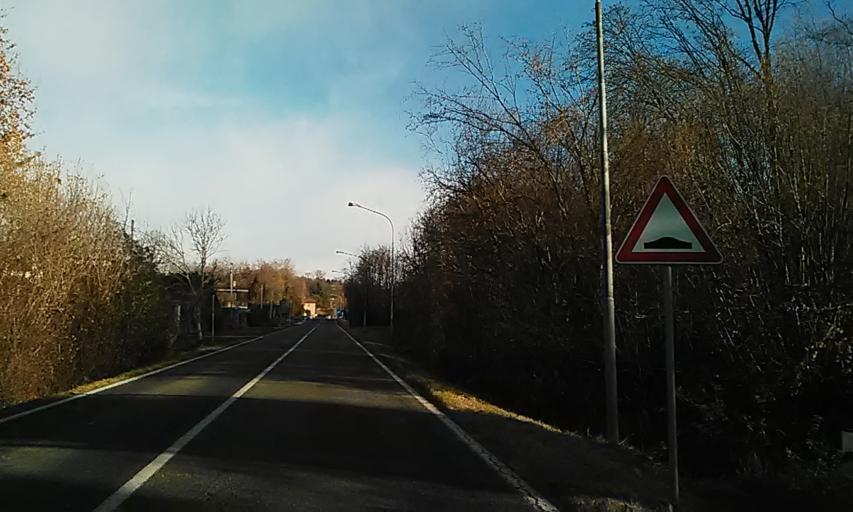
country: IT
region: Piedmont
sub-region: Provincia di Vercelli
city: Roasio
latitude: 45.5903
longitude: 8.2726
